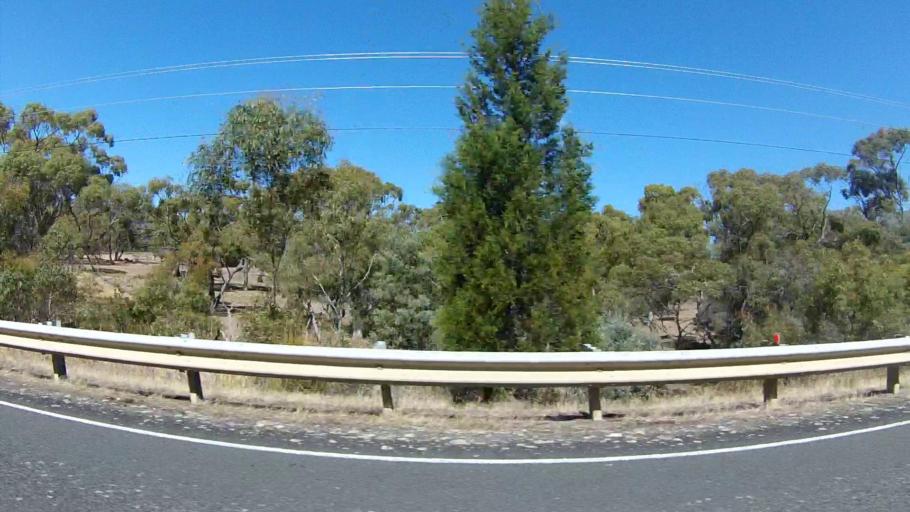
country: AU
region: Tasmania
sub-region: Sorell
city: Sorell
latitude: -42.5828
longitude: 147.8103
